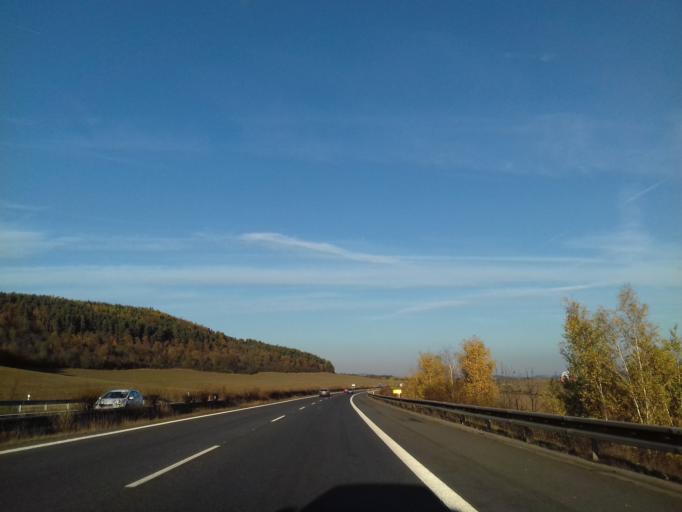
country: CZ
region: Central Bohemia
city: Zebrak
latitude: 49.8837
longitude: 13.9159
